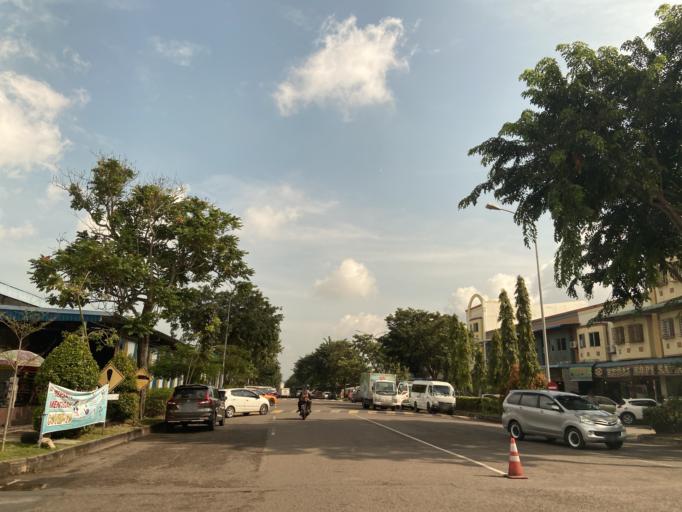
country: SG
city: Singapore
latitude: 1.1052
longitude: 104.0722
